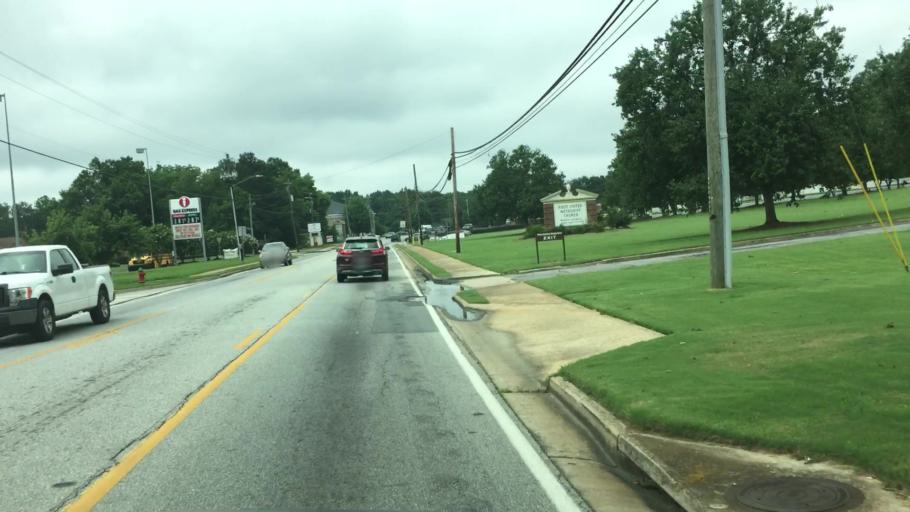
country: US
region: Georgia
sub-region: Barrow County
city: Winder
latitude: 34.0046
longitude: -83.7069
